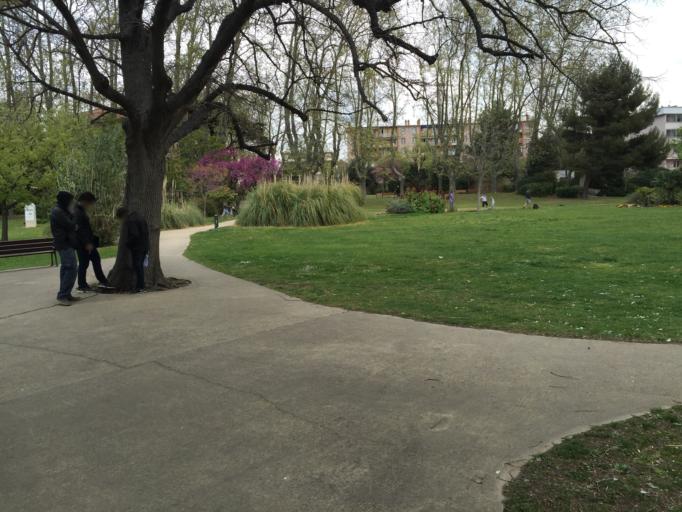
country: FR
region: Provence-Alpes-Cote d'Azur
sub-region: Departement des Bouches-du-Rhone
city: Marseille 09
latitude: 43.2476
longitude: 5.3960
